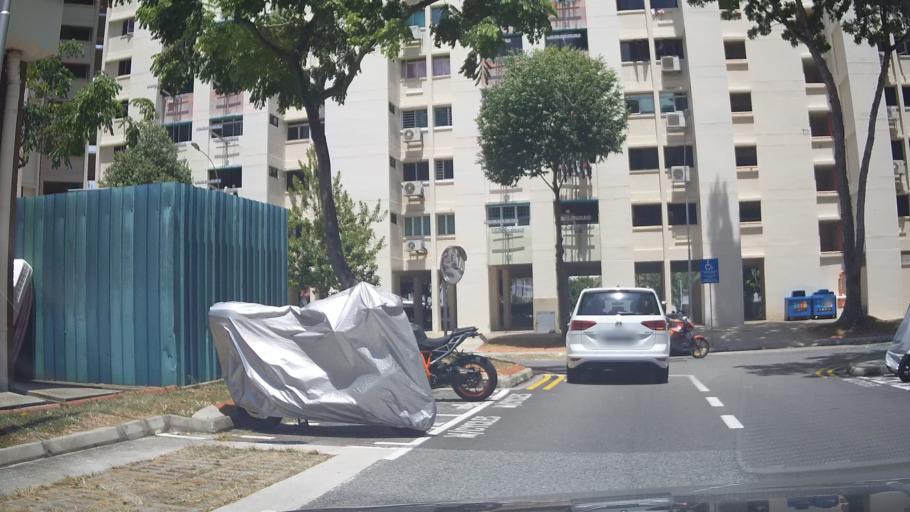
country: SG
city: Singapore
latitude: 1.3579
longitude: 103.9541
